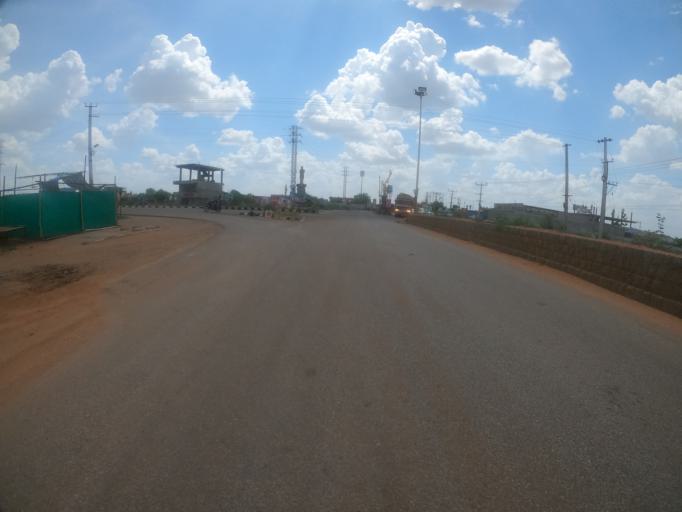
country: IN
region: Telangana
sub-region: Rangareddi
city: Sriramnagar
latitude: 17.3054
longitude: 78.1465
